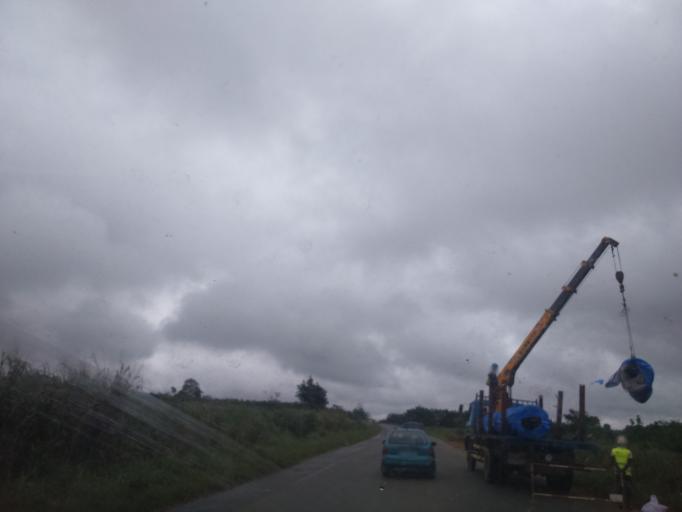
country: CI
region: Sud-Comoe
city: Bonoua
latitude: 5.2761
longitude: -3.5678
